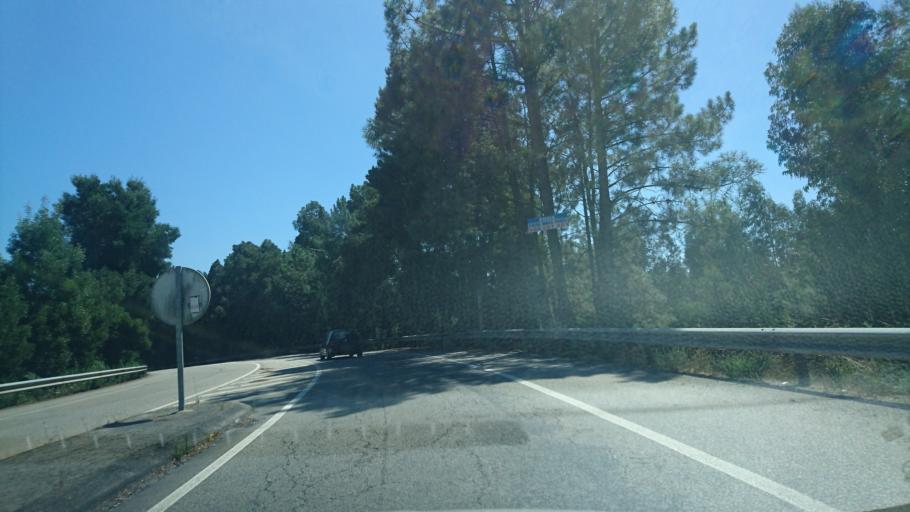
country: PT
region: Aveiro
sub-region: Espinho
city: Souto
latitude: 40.9706
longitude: -8.6113
